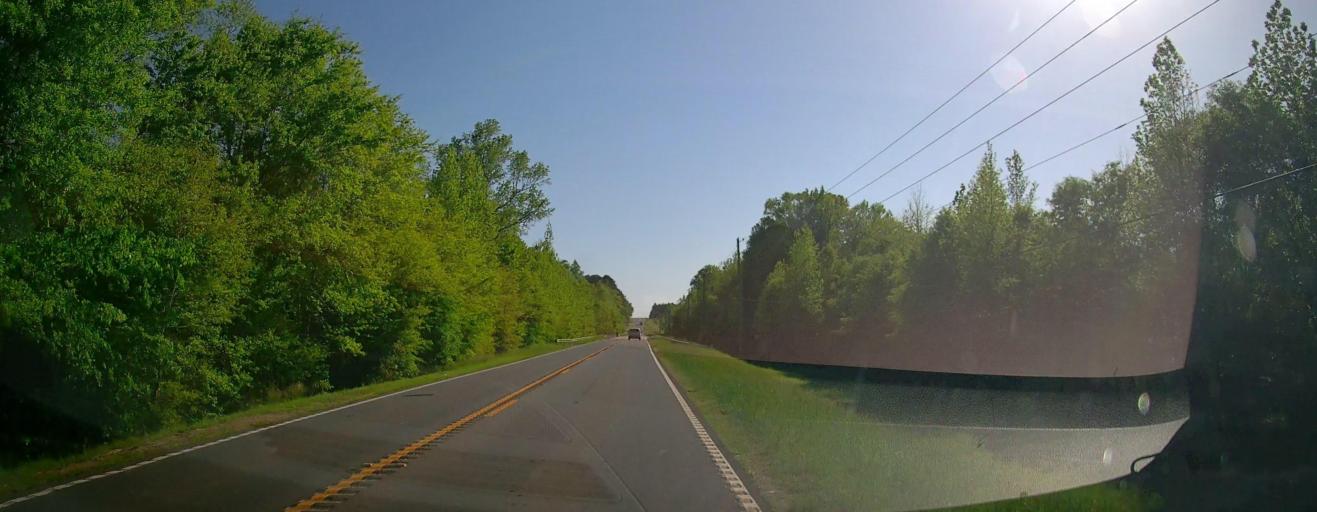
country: US
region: Georgia
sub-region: Houston County
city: Perry
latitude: 32.4528
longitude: -83.6224
